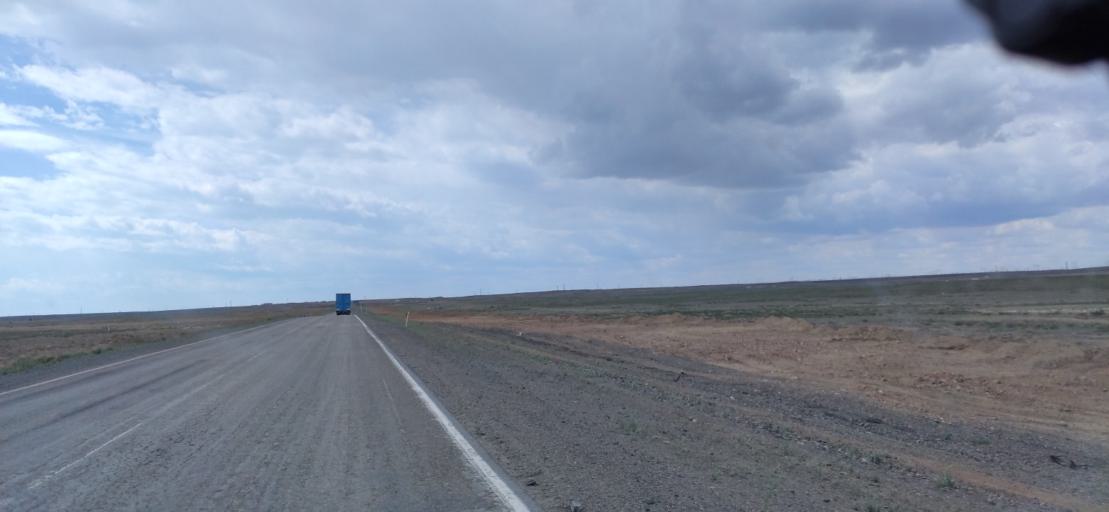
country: KZ
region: Qaraghandy
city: Saryshaghan
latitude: 46.0529
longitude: 73.5969
